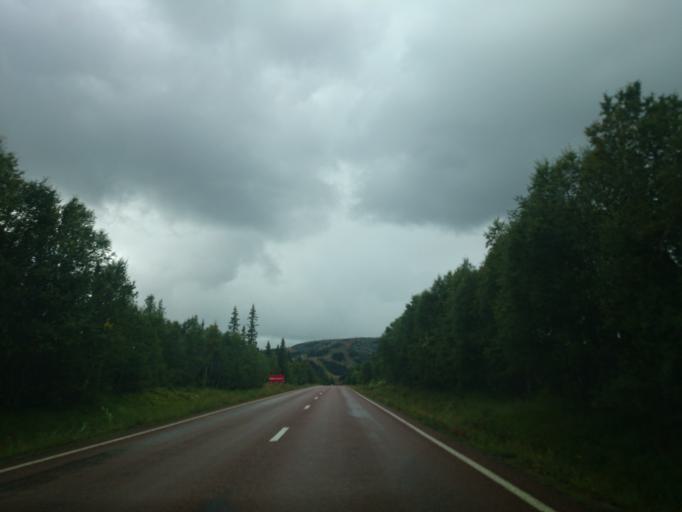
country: SE
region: Jaemtland
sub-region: Bergs Kommun
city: Hoverberg
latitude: 62.4809
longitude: 13.9971
